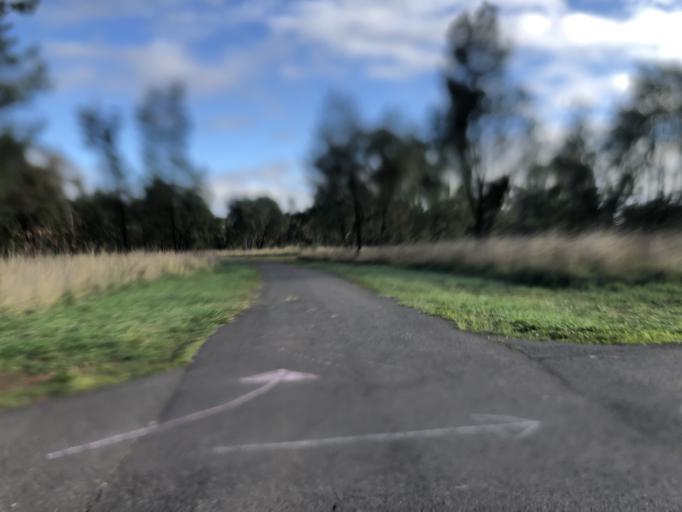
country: AU
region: New South Wales
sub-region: Orange Municipality
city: Orange
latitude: -33.3265
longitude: 149.0871
